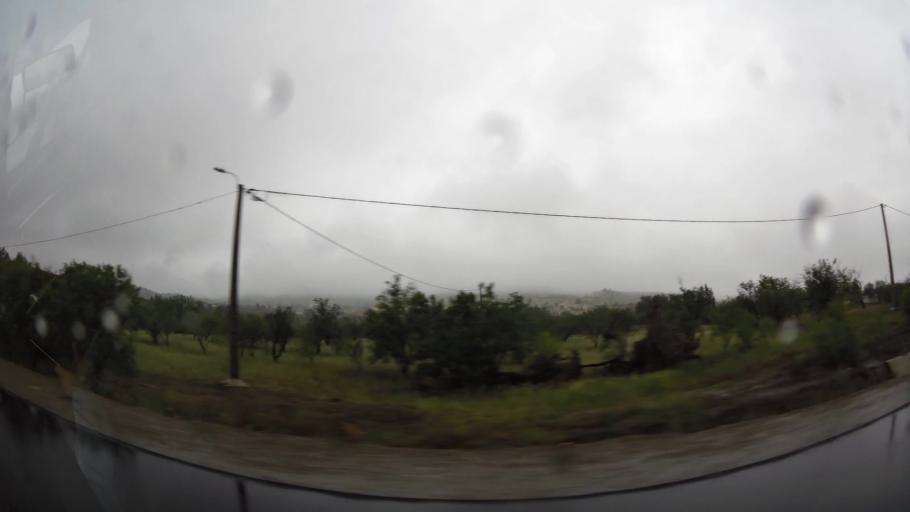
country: MA
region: Oriental
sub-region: Nador
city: Midar
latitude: 34.8551
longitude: -3.7221
